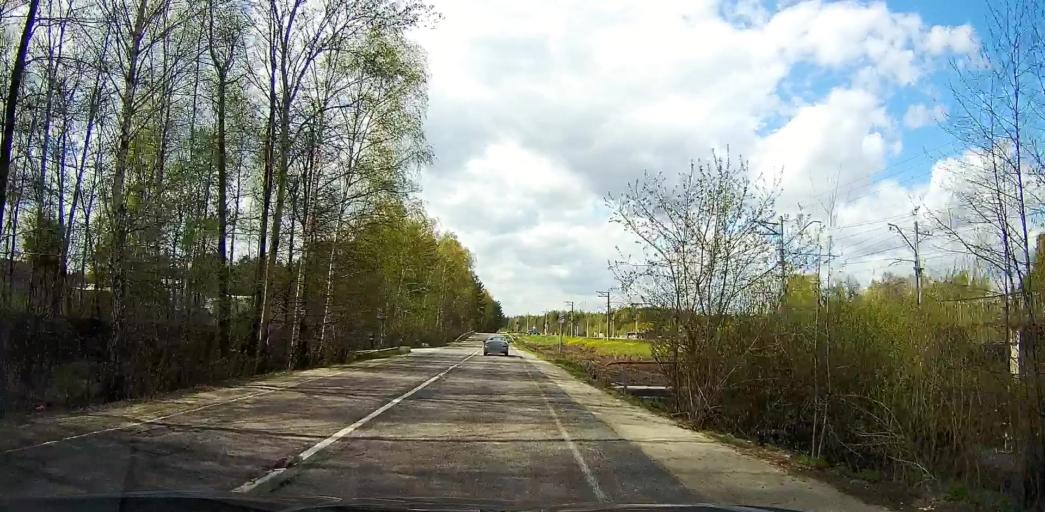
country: RU
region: Moskovskaya
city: Davydovo
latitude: 55.5723
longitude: 38.8214
